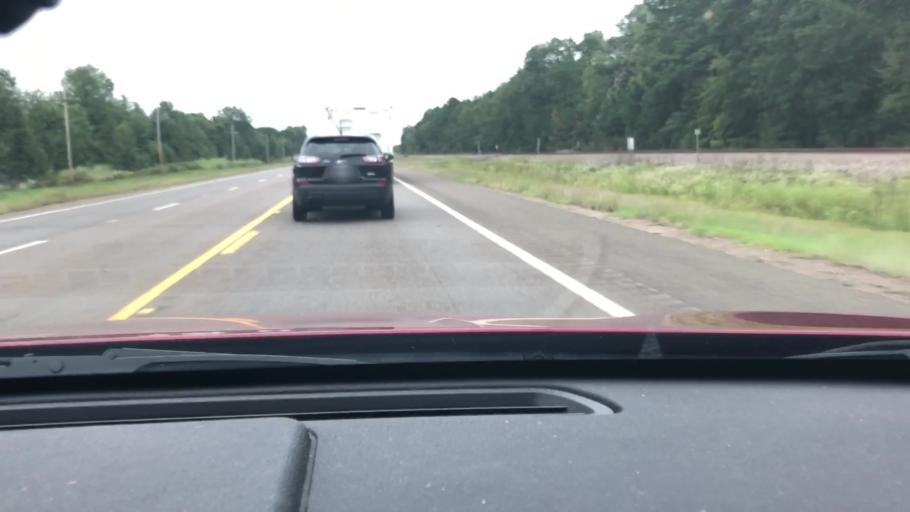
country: US
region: Arkansas
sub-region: Lafayette County
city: Lewisville
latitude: 33.3574
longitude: -93.5985
